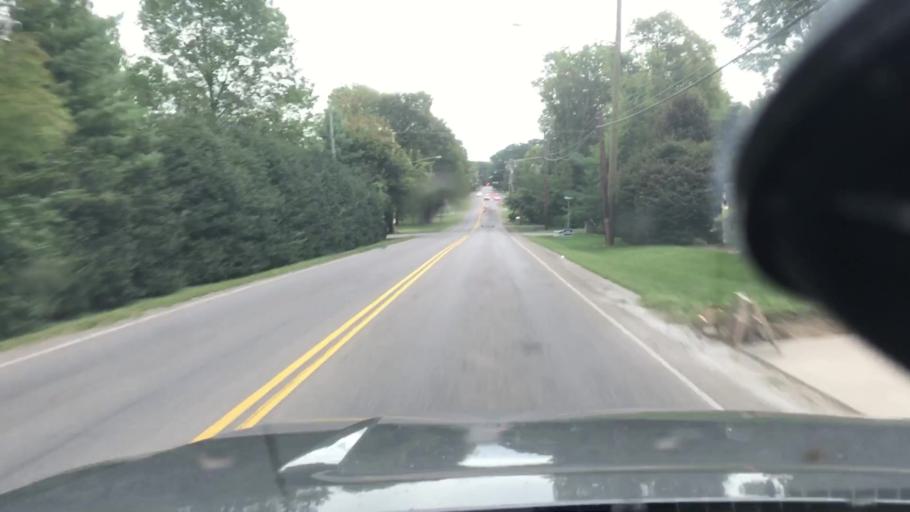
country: US
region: Tennessee
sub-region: Davidson County
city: Oak Hill
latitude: 36.1134
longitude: -86.8040
